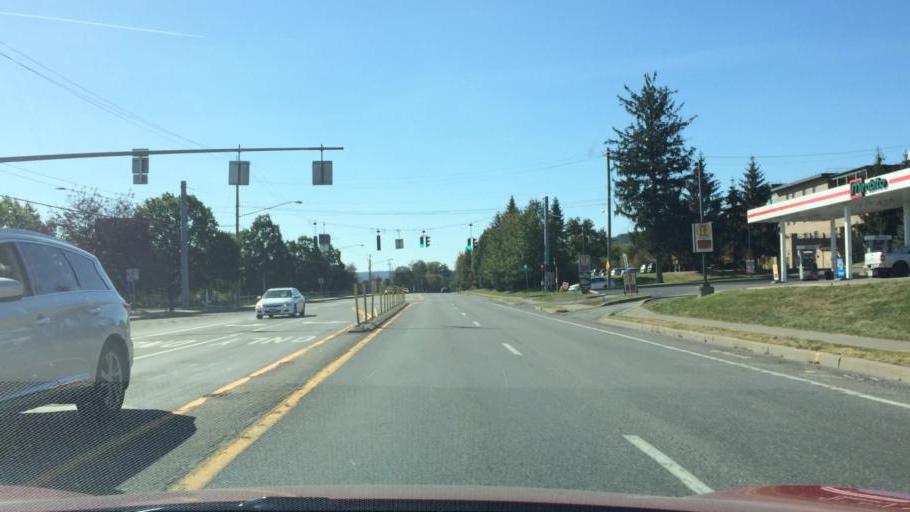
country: US
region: New York
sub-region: Broome County
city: Port Dickinson
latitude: 42.1326
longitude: -75.9057
